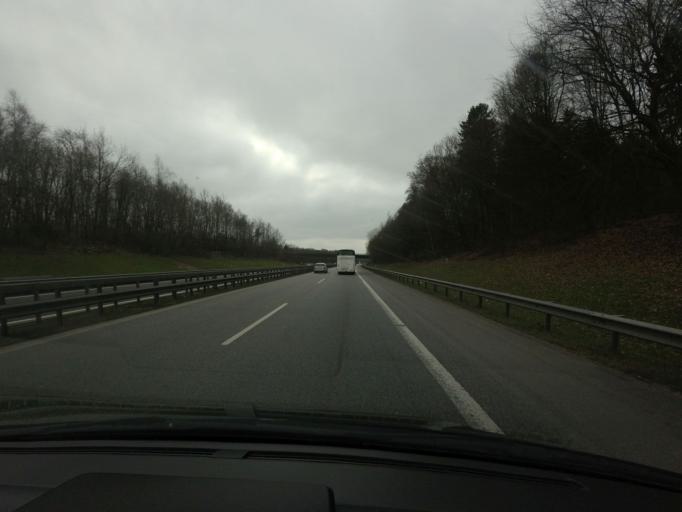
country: DE
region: Lower Saxony
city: Seevetal
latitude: 53.4282
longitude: 9.9280
